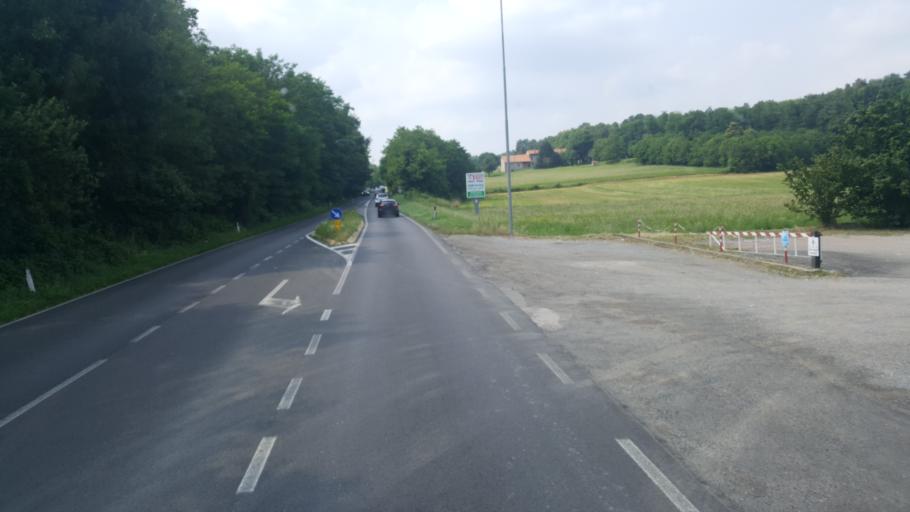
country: IT
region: Lombardy
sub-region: Provincia di Como
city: Oltrona di San Mamette
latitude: 45.7577
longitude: 8.9665
